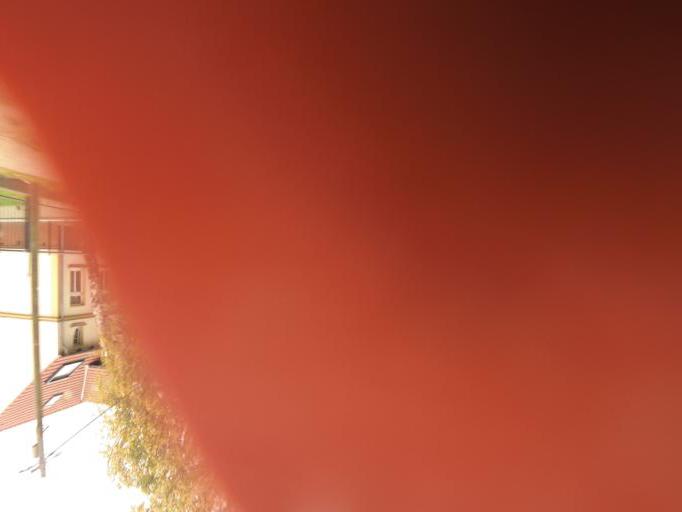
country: DE
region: Saxony-Anhalt
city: Kretzschau
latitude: 51.0595
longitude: 12.0729
